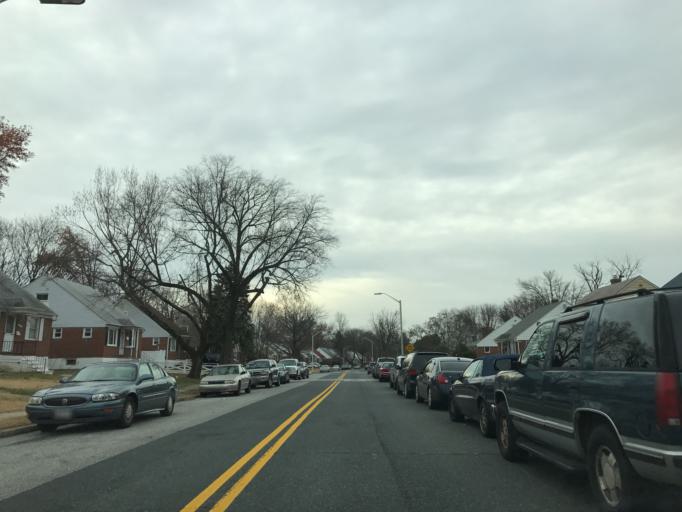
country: US
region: Maryland
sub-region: Baltimore County
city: Parkville
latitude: 39.3568
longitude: -76.5471
